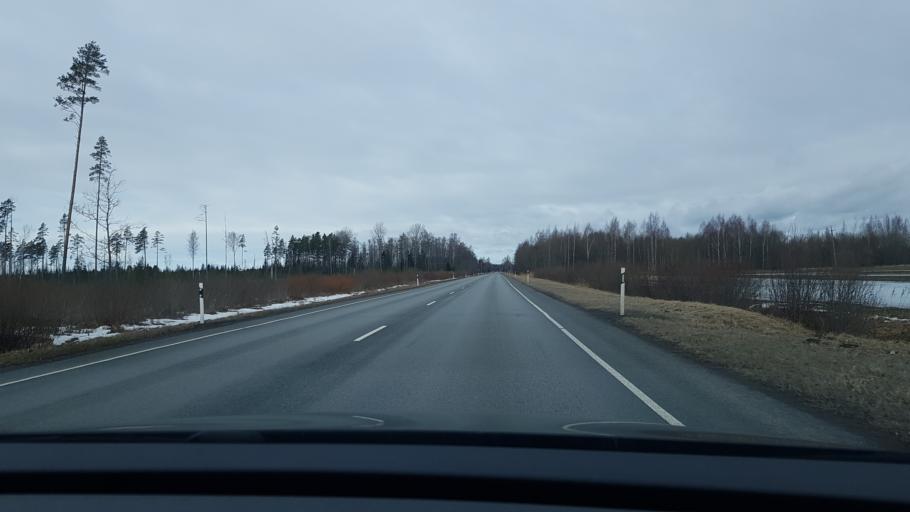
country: EE
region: Paernumaa
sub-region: Paikuse vald
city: Paikuse
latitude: 58.2202
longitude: 24.7075
